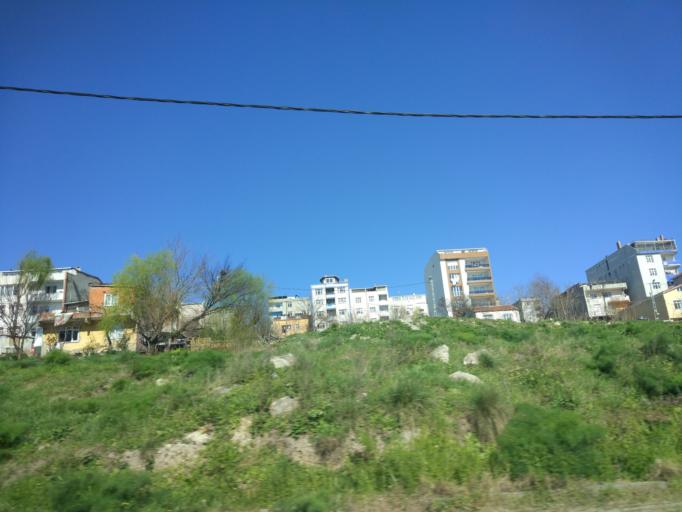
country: TR
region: Istanbul
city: Basaksehir
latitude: 41.0464
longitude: 28.7493
